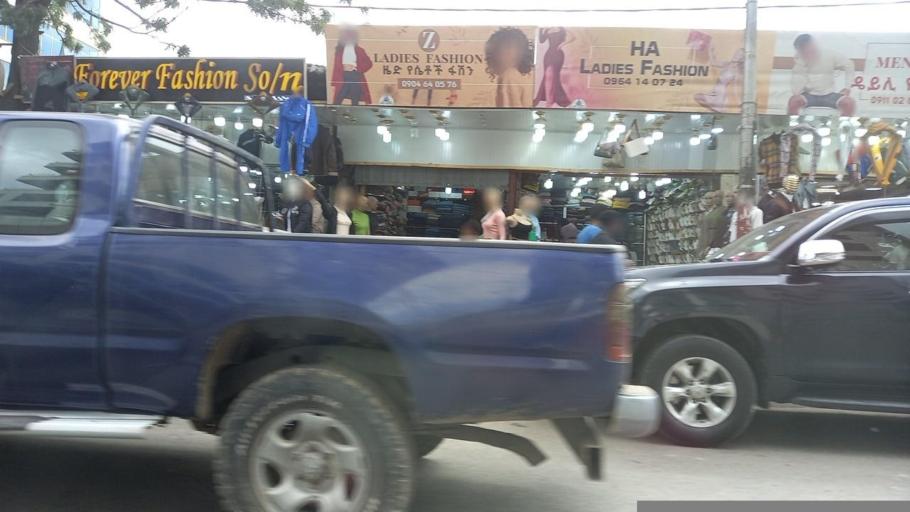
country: ET
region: Adis Abeba
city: Addis Ababa
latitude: 9.0207
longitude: 38.7979
